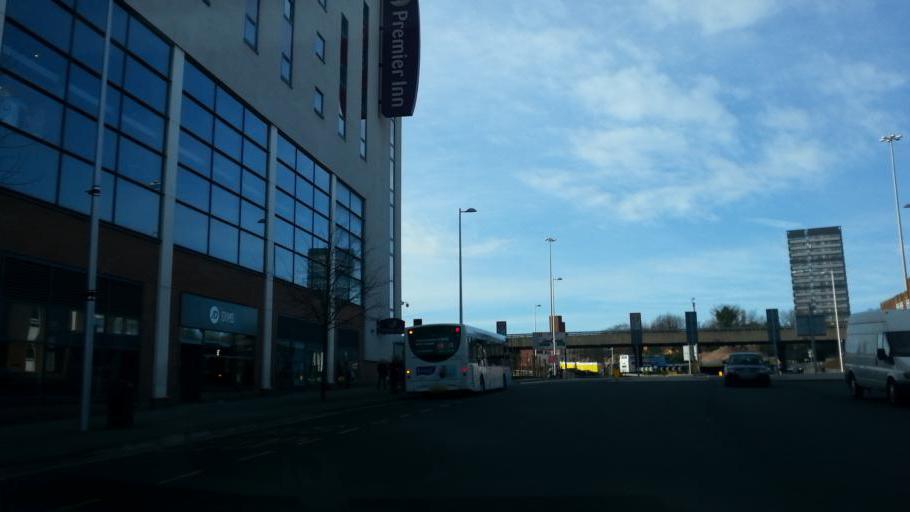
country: GB
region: England
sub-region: Coventry
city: Coventry
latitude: 52.4105
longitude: -1.5140
